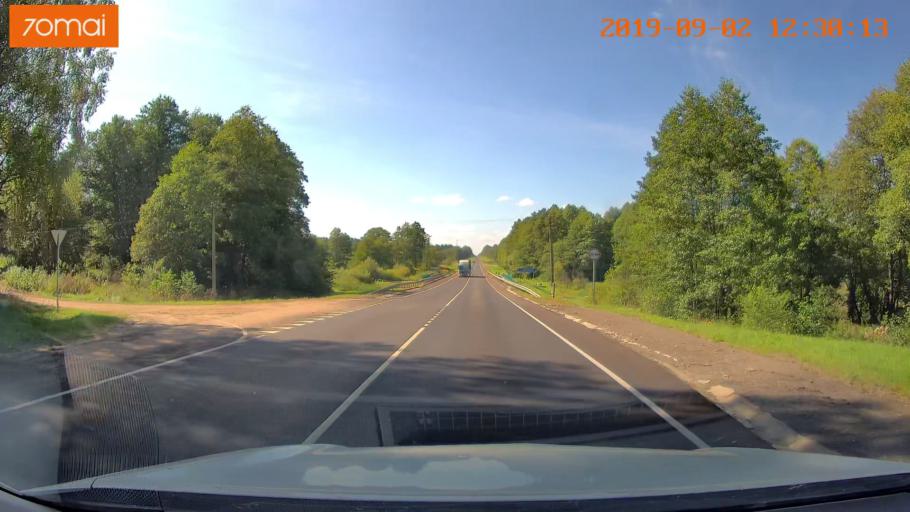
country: RU
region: Smolensk
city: Shumyachi
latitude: 53.8336
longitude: 32.4793
